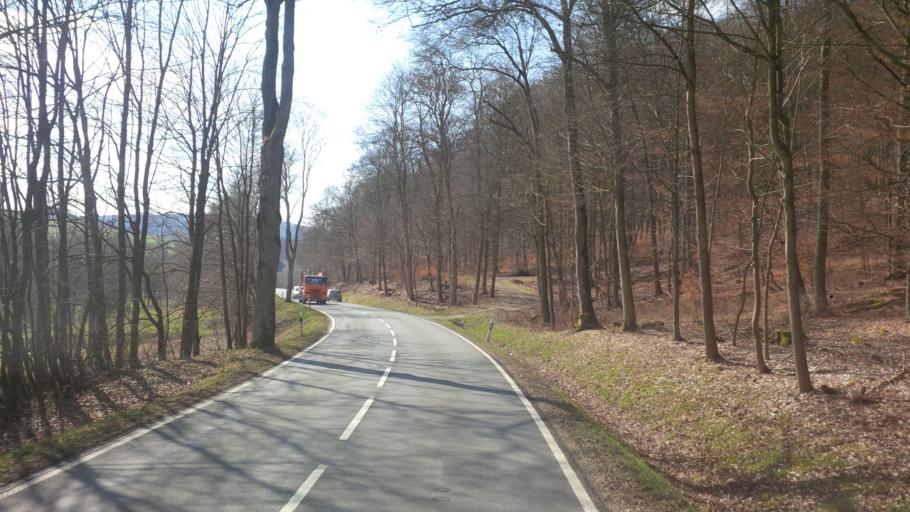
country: DE
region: Hesse
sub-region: Regierungsbezirk Darmstadt
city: Schmitten
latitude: 50.2965
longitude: 8.4620
